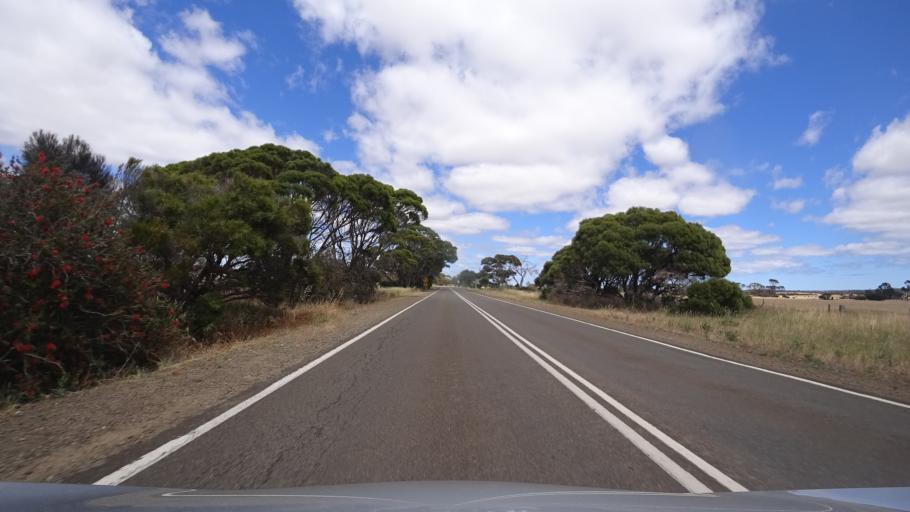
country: AU
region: South Australia
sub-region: Kangaroo Island
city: Kingscote
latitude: -35.6819
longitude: 137.5511
